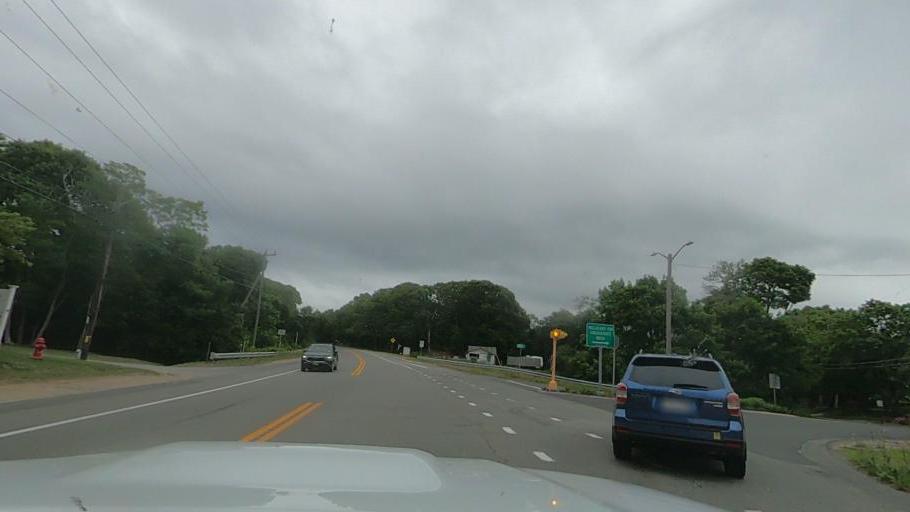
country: US
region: Massachusetts
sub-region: Barnstable County
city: Wellfleet
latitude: 41.9460
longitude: -70.0317
